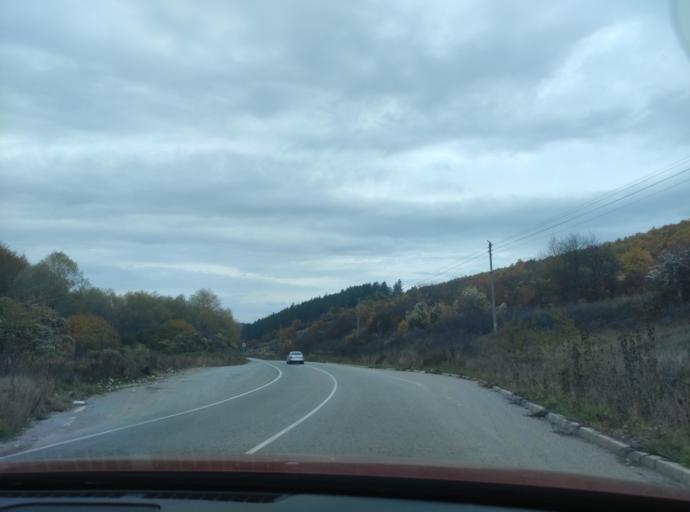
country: BG
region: Sofiya
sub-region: Obshtina Godech
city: Godech
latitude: 42.9668
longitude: 23.1496
